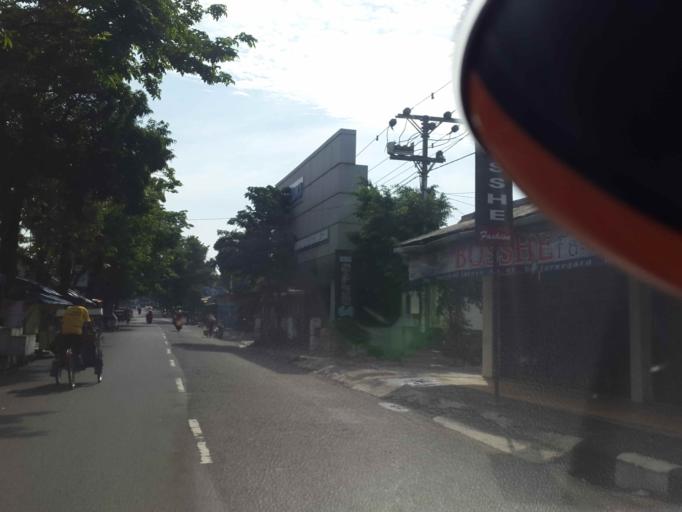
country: ID
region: Central Java
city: Wonosobo
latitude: -7.3929
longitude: 109.6978
